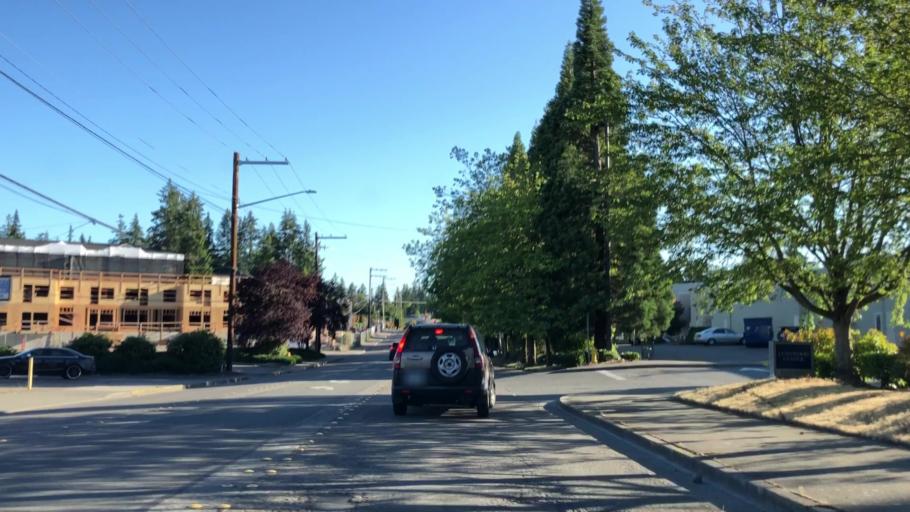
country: US
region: Washington
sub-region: Snohomish County
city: Lynnwood
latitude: 47.8201
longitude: -122.3119
